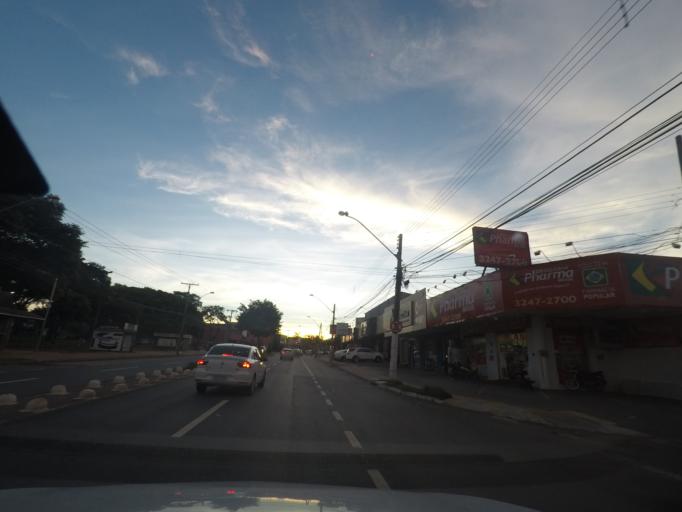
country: BR
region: Goias
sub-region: Goiania
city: Goiania
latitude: -16.6961
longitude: -49.3006
